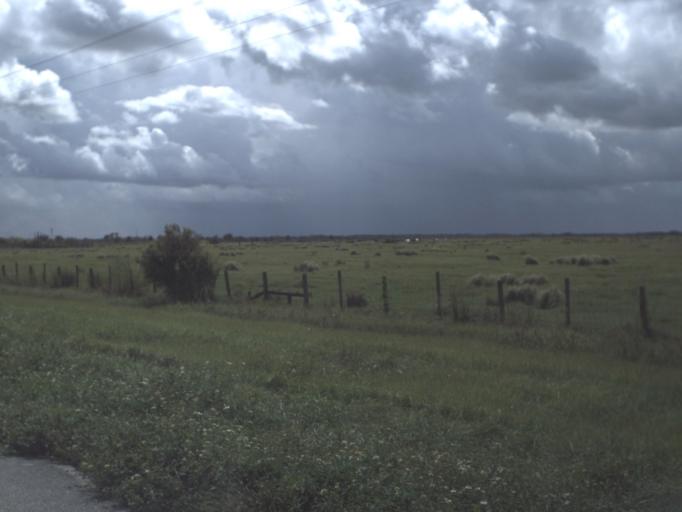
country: US
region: Florida
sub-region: Okeechobee County
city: Okeechobee
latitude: 27.3519
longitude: -80.9545
